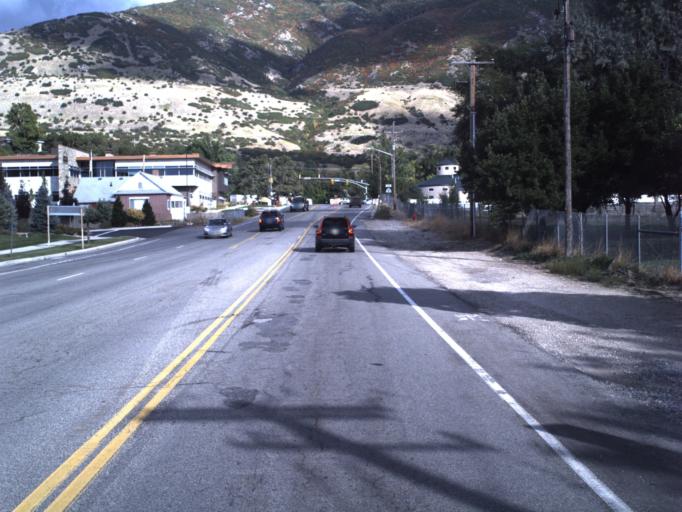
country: US
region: Utah
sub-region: Davis County
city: Farmington
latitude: 40.9914
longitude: -111.8963
